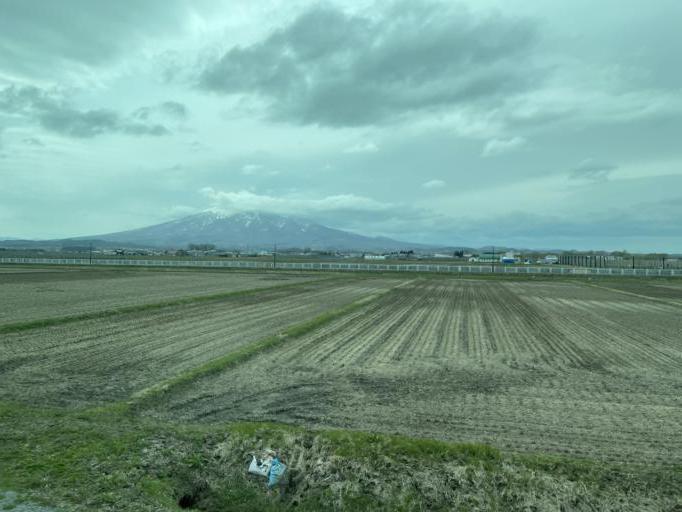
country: JP
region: Aomori
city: Goshogawara
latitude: 40.7428
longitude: 140.4350
